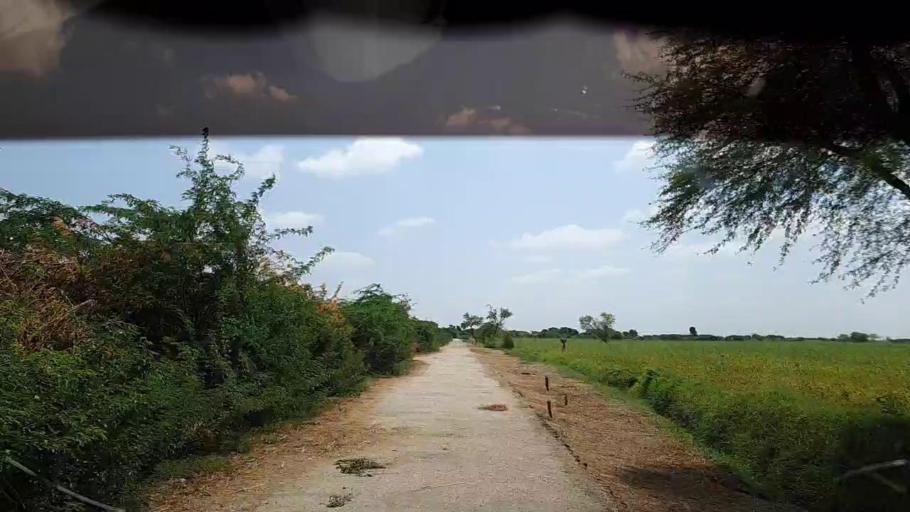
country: PK
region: Sindh
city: Kadhan
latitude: 24.5845
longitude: 68.9603
